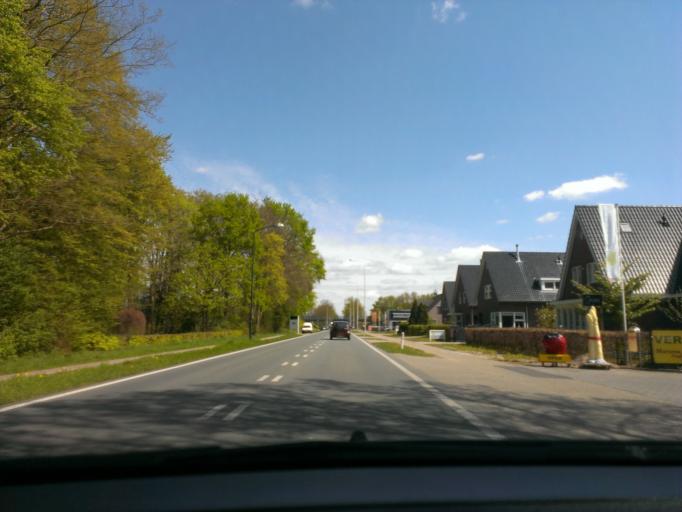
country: NL
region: Gelderland
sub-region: Gemeente Apeldoorn
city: Apeldoorn
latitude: 52.2260
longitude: 6.0131
